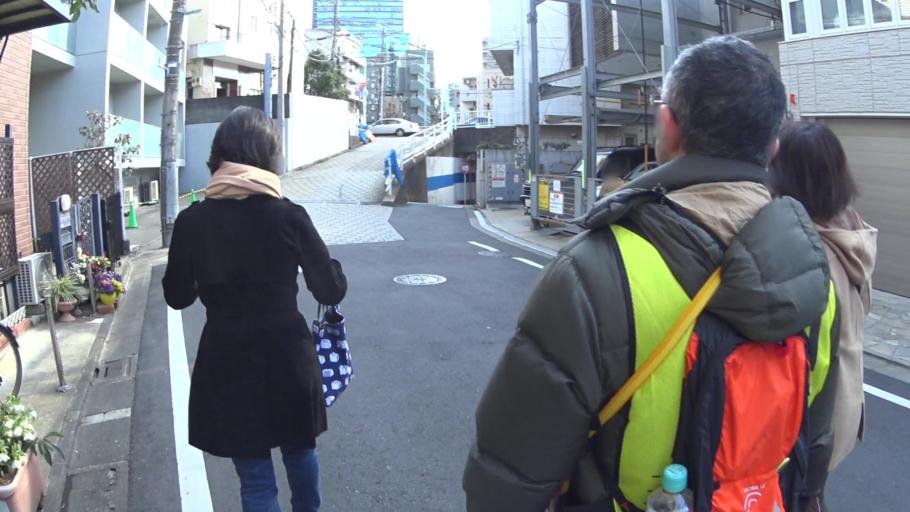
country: JP
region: Tokyo
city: Tokyo
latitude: 35.6559
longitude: 139.6899
